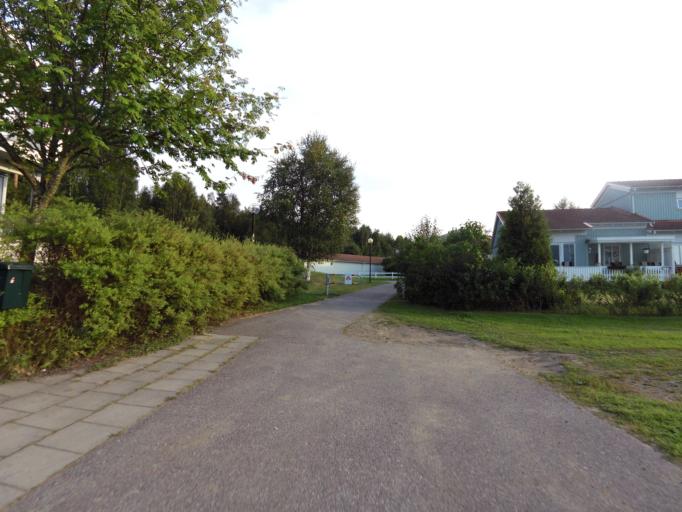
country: SE
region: Gaevleborg
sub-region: Gavle Kommun
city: Gavle
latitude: 60.7024
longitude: 17.1034
